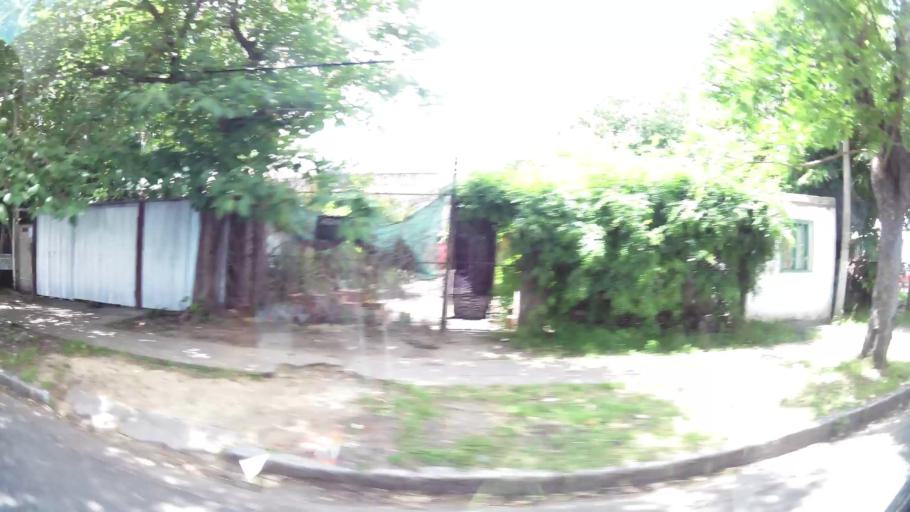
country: AR
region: Santa Fe
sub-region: Departamento de Rosario
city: Rosario
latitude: -32.9704
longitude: -60.6338
